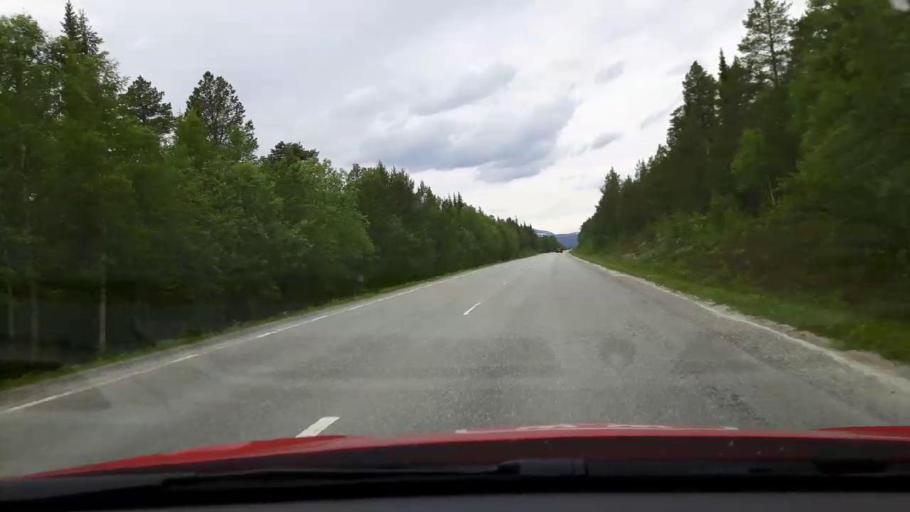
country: NO
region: Hedmark
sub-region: Engerdal
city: Engerdal
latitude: 62.5261
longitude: 12.5807
